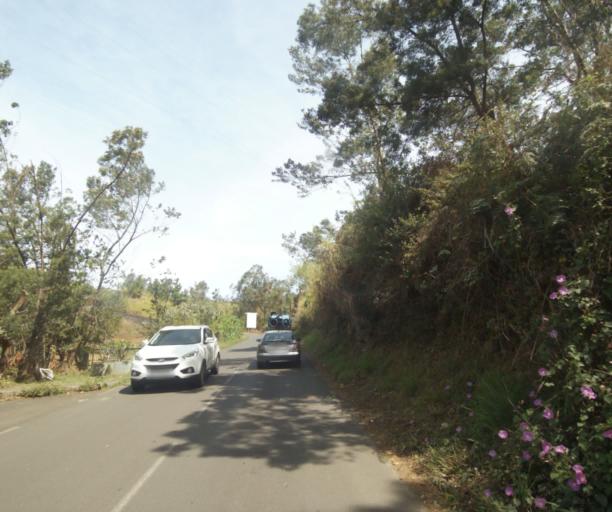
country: RE
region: Reunion
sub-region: Reunion
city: Saint-Paul
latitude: -21.0401
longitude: 55.3175
